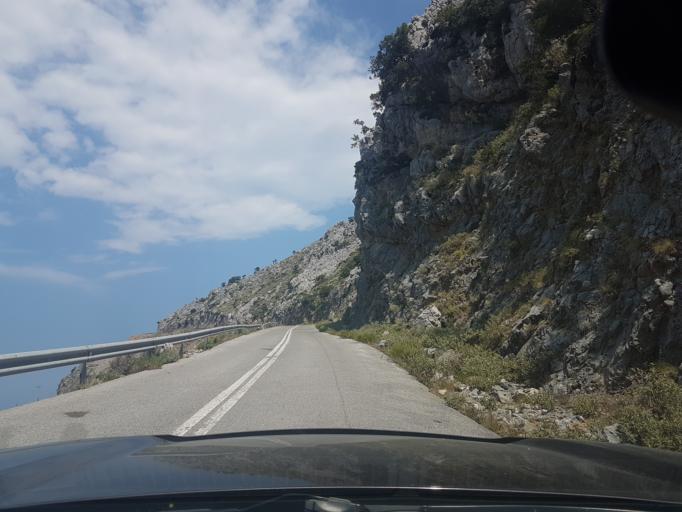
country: GR
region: Central Greece
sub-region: Nomos Evvoias
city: Kymi
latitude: 38.6545
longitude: 23.9650
